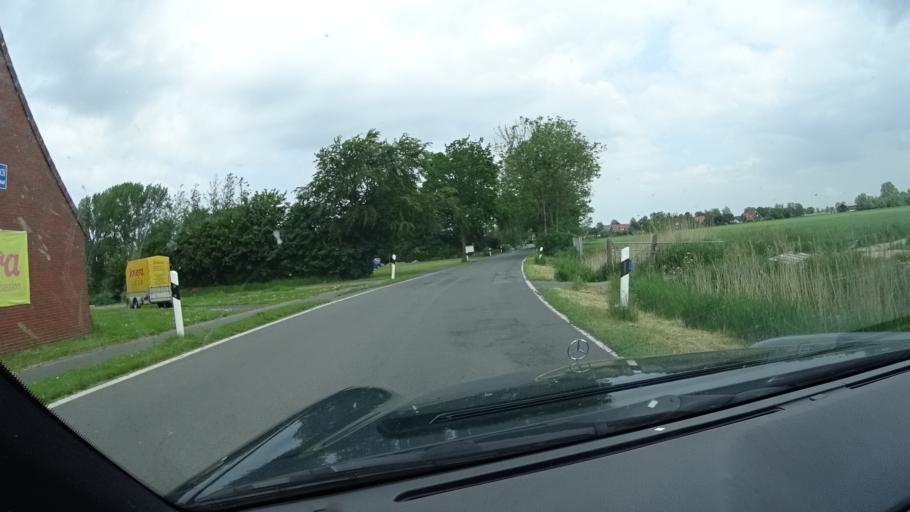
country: DE
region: Lower Saxony
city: Butjadingen
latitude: 53.5869
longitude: 8.2727
